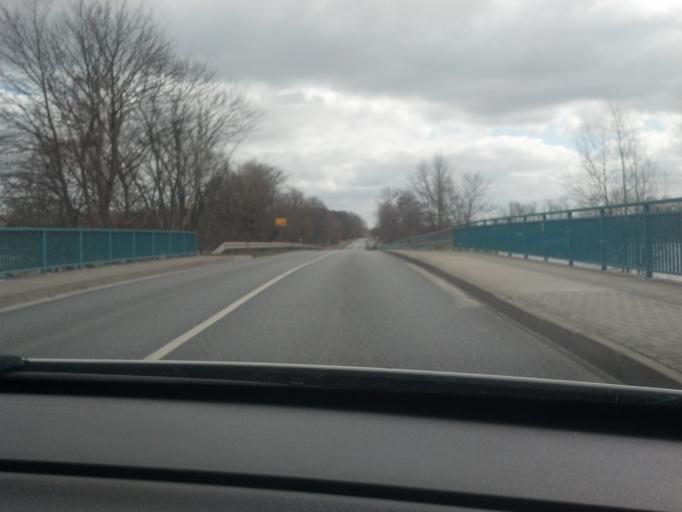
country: DE
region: Mecklenburg-Vorpommern
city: Rechlin
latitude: 53.3244
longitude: 12.6943
